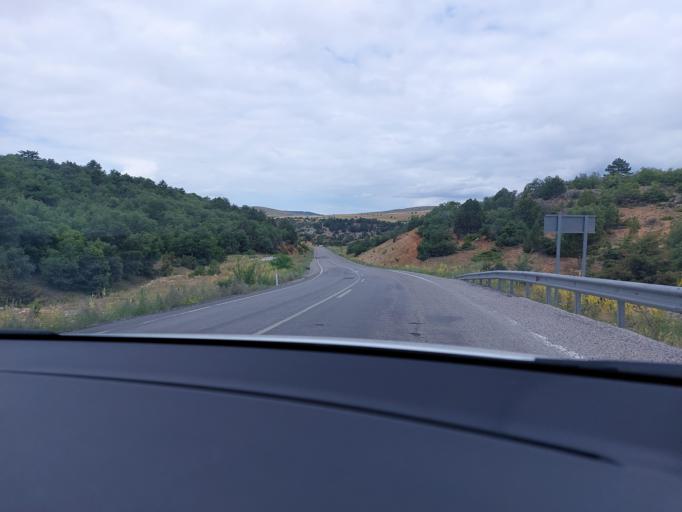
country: TR
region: Konya
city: Doganbey
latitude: 37.8980
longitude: 31.8118
